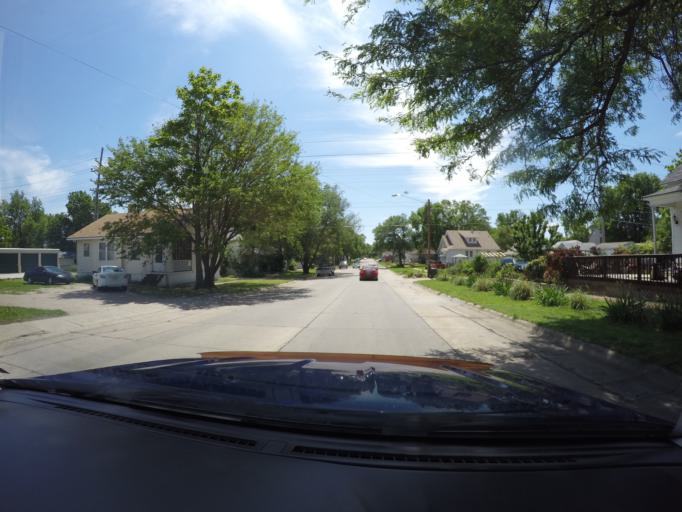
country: US
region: Nebraska
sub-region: Hall County
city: Grand Island
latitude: 40.9266
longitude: -98.3349
